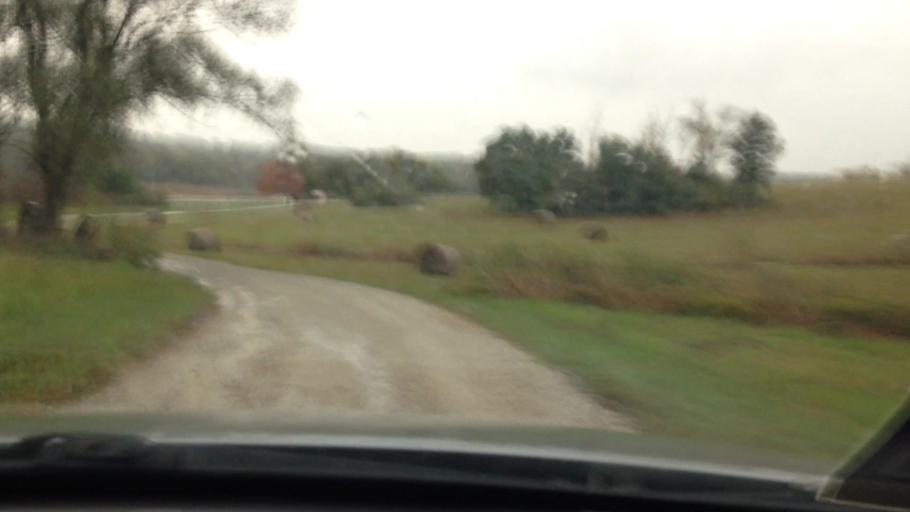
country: US
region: Missouri
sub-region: Platte County
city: Weston
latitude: 39.3894
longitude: -94.8512
